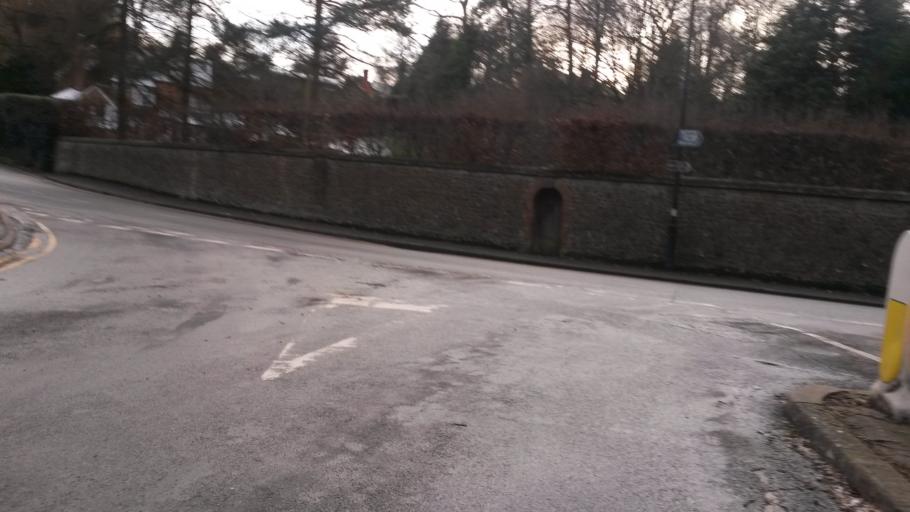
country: GB
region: England
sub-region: Surrey
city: Haslemere
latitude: 51.0890
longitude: -0.7150
